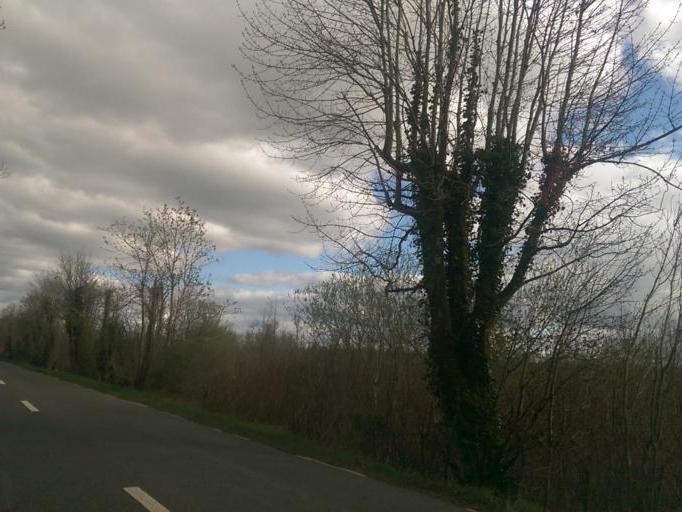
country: IE
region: Connaught
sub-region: County Galway
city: Ballinasloe
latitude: 53.4199
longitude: -8.3886
